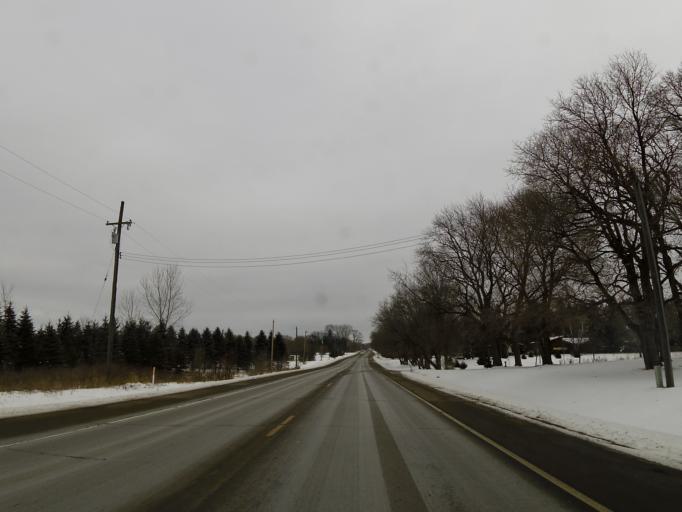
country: US
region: Minnesota
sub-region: Washington County
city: Lake Elmo
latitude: 45.0072
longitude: -92.8480
